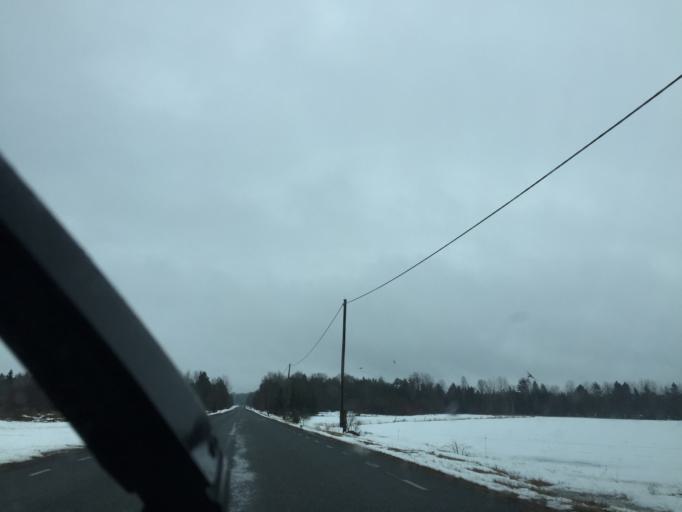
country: EE
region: Saare
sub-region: Kuressaare linn
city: Kuressaare
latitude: 58.3437
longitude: 22.0303
